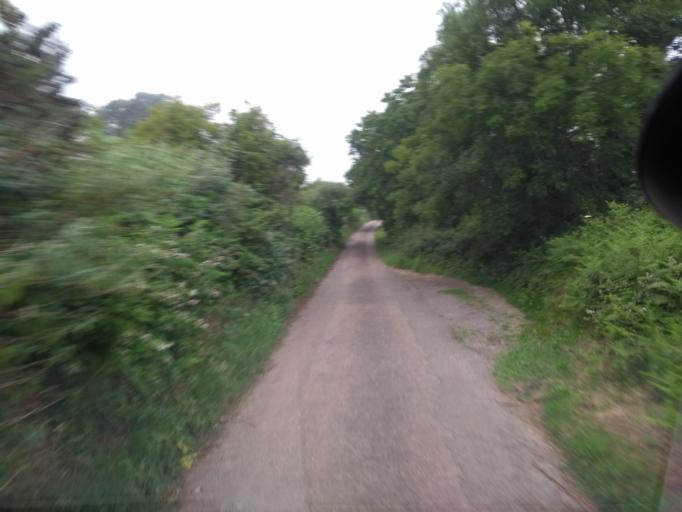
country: GB
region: England
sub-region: Dorset
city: Bridport
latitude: 50.7313
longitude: -2.7962
